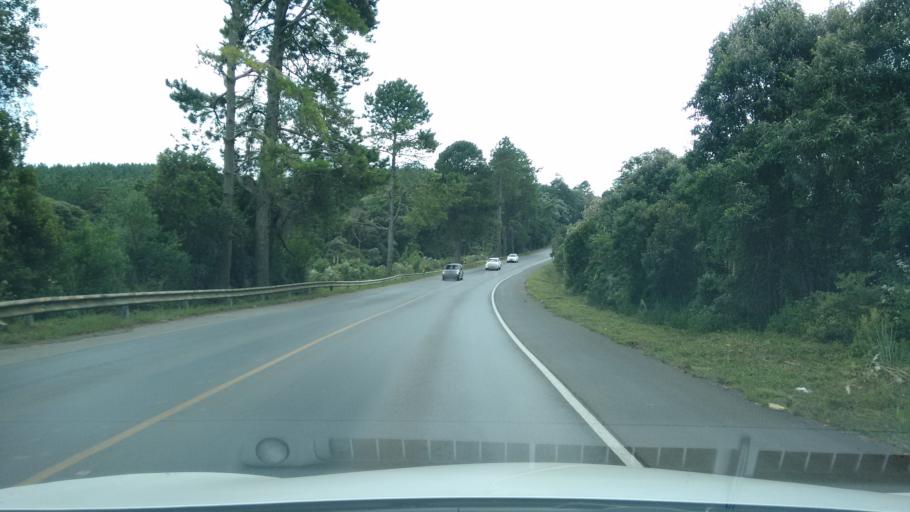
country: BR
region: Santa Catarina
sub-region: Curitibanos
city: Curitibanos
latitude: -27.3216
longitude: -50.3379
